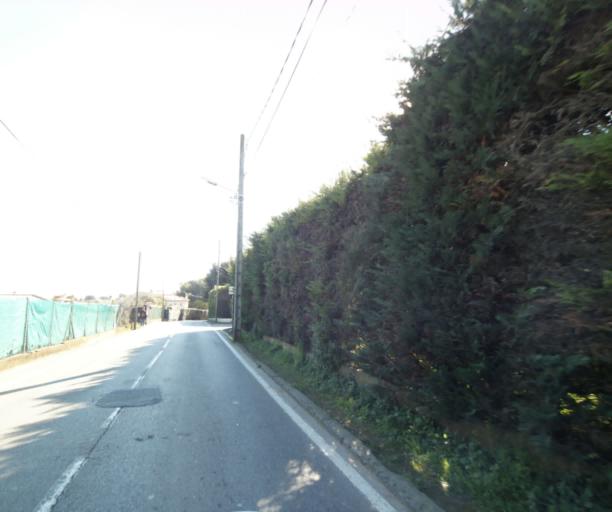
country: FR
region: Provence-Alpes-Cote d'Azur
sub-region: Departement des Alpes-Maritimes
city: Biot
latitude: 43.6072
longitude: 7.0879
